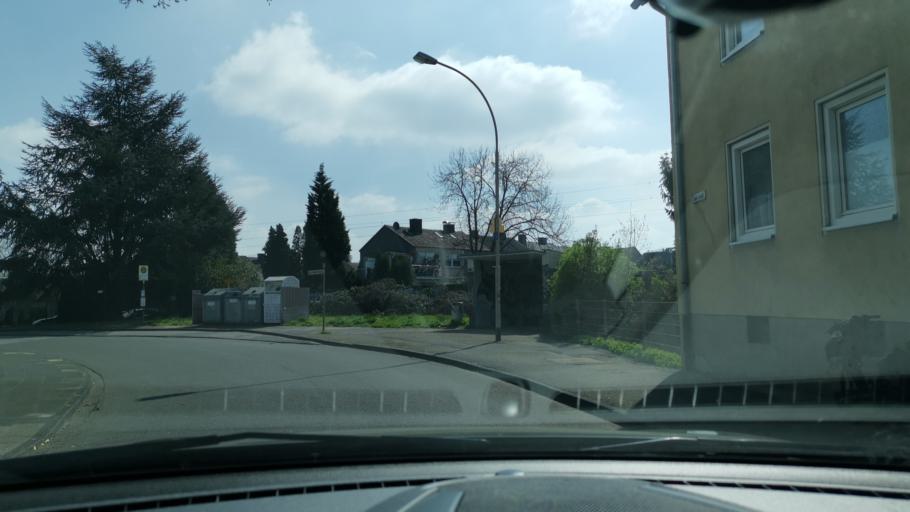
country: DE
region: North Rhine-Westphalia
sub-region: Regierungsbezirk Dusseldorf
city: Grevenbroich
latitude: 51.0848
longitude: 6.6005
